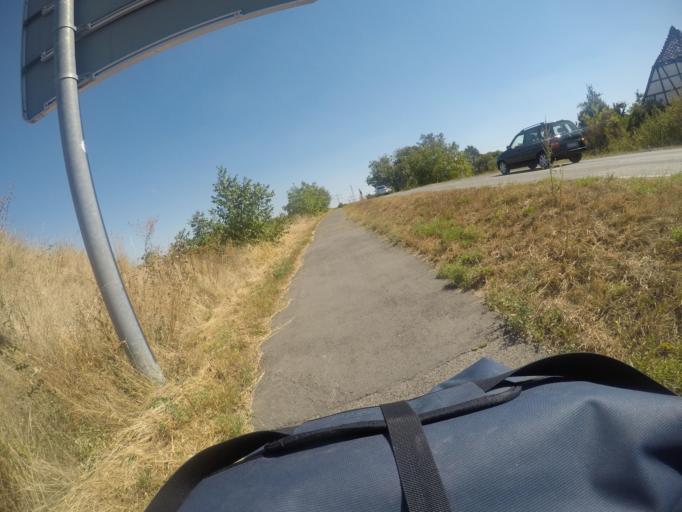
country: DE
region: Baden-Wuerttemberg
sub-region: Karlsruhe Region
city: Philippsburg
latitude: 49.2328
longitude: 8.4686
